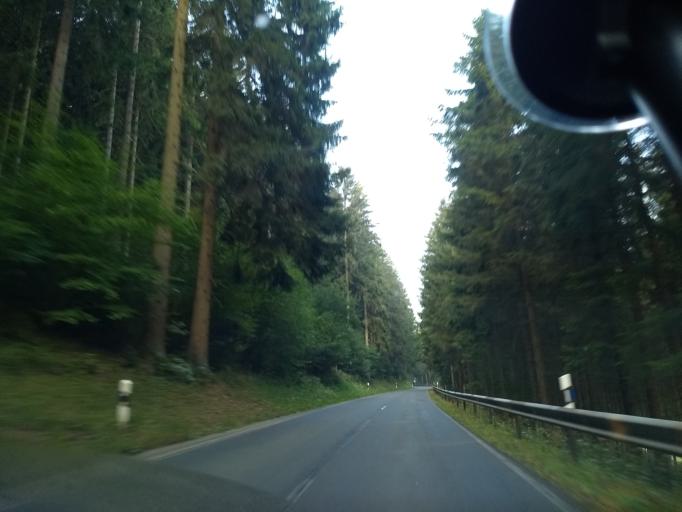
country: DE
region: North Rhine-Westphalia
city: Eslohe
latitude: 51.2286
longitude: 8.1229
